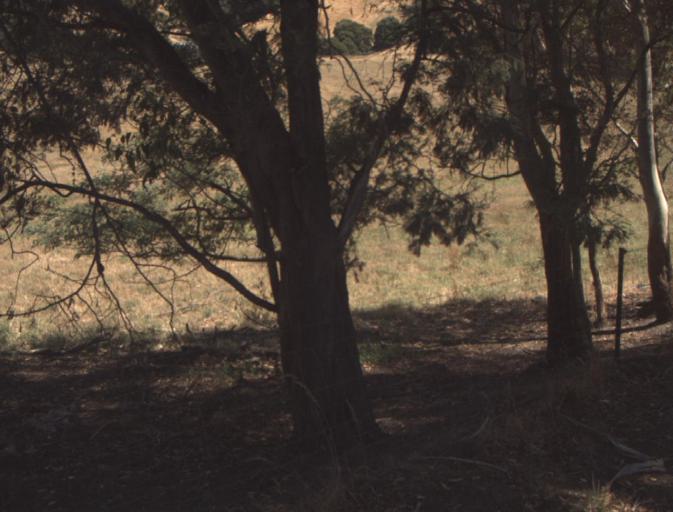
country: AU
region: Tasmania
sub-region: Launceston
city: Mayfield
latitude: -41.2723
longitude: 147.1271
